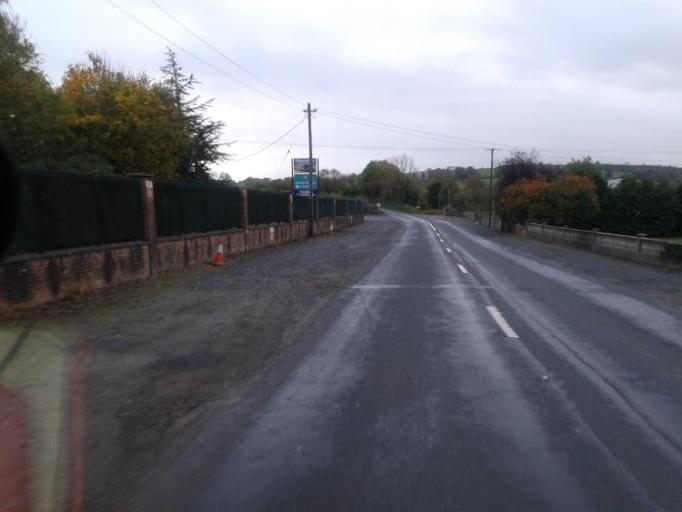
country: IE
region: Munster
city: Ballina
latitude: 52.7748
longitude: -8.4310
